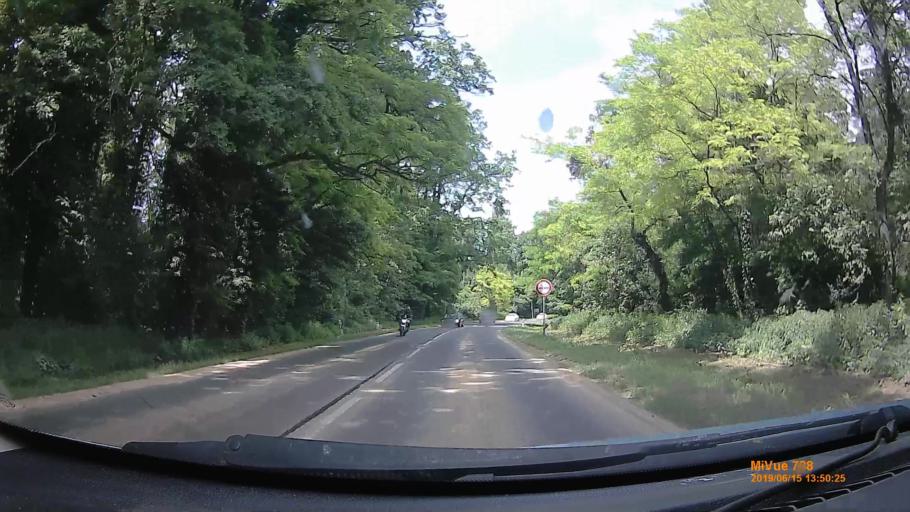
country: HU
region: Tolna
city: Iregszemcse
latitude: 46.7426
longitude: 18.1616
